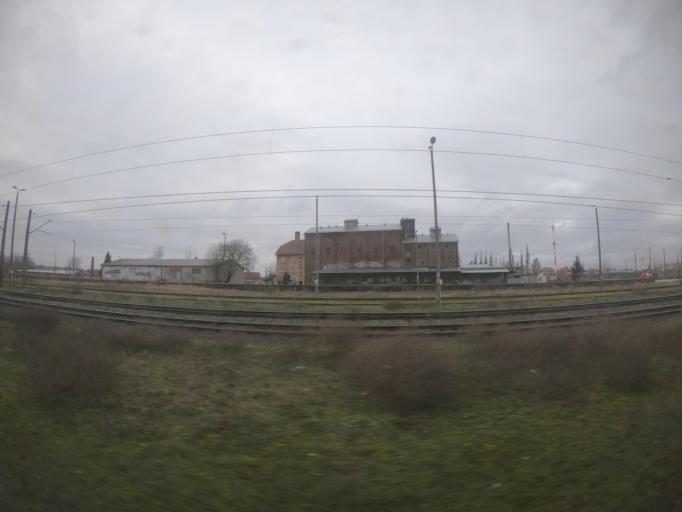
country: PL
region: West Pomeranian Voivodeship
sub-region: Powiat szczecinecki
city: Szczecinek
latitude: 53.6964
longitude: 16.7100
